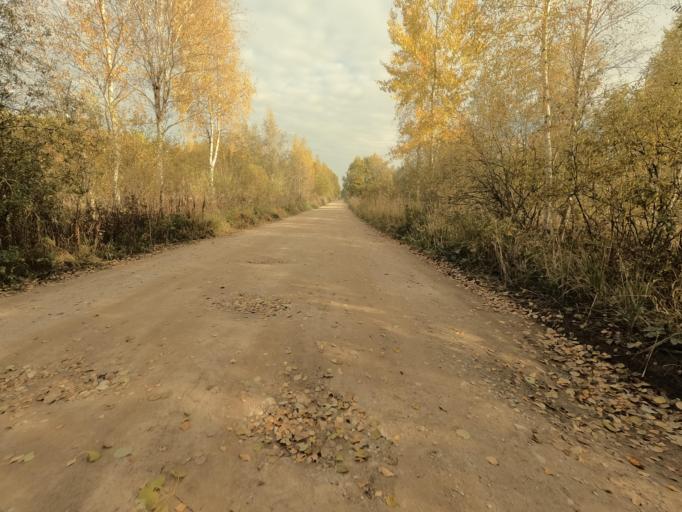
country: RU
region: Novgorod
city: Pankovka
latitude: 58.8947
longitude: 31.0139
